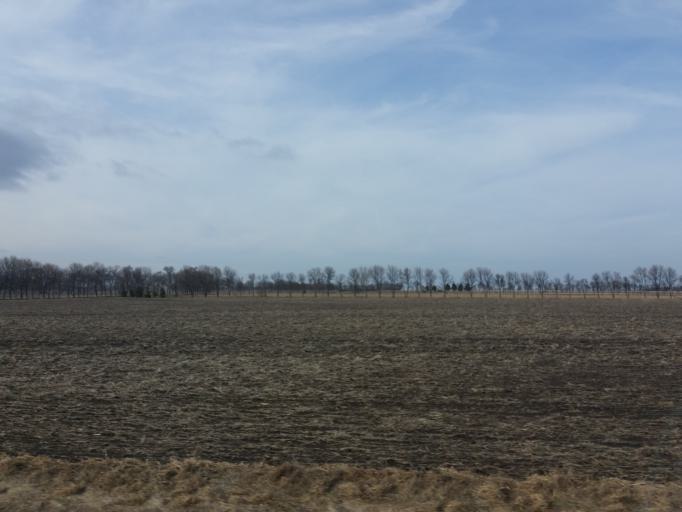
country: US
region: North Dakota
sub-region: Richland County
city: Wahpeton
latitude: 46.4711
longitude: -96.6442
